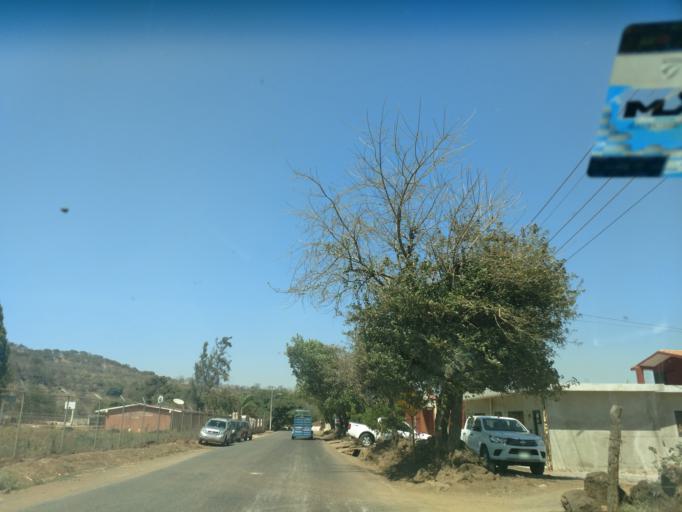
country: MX
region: Nayarit
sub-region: Tepic
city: La Corregidora
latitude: 21.5046
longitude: -104.7111
